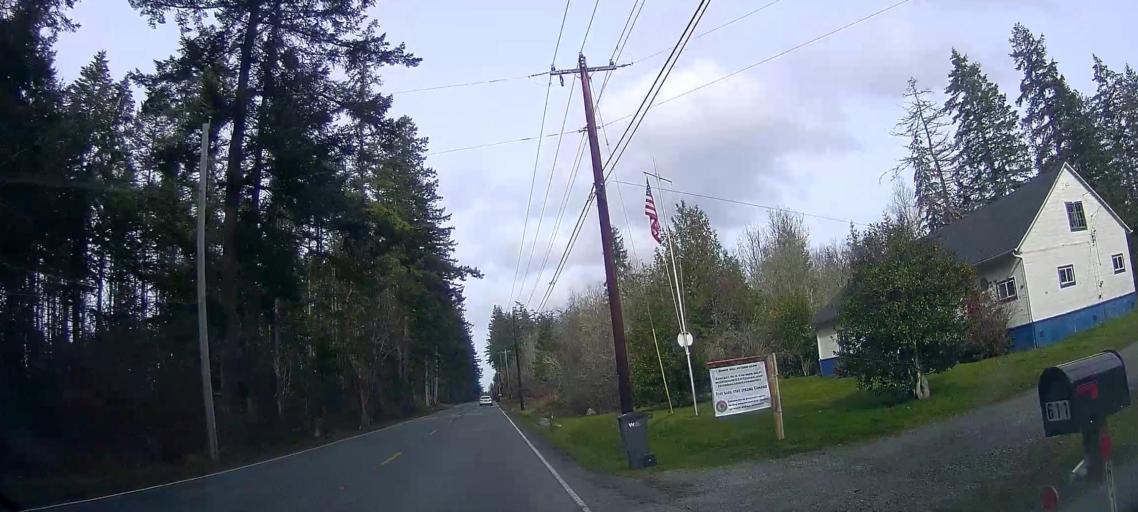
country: US
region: Washington
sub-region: Island County
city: Camano
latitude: 48.1892
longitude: -122.5273
